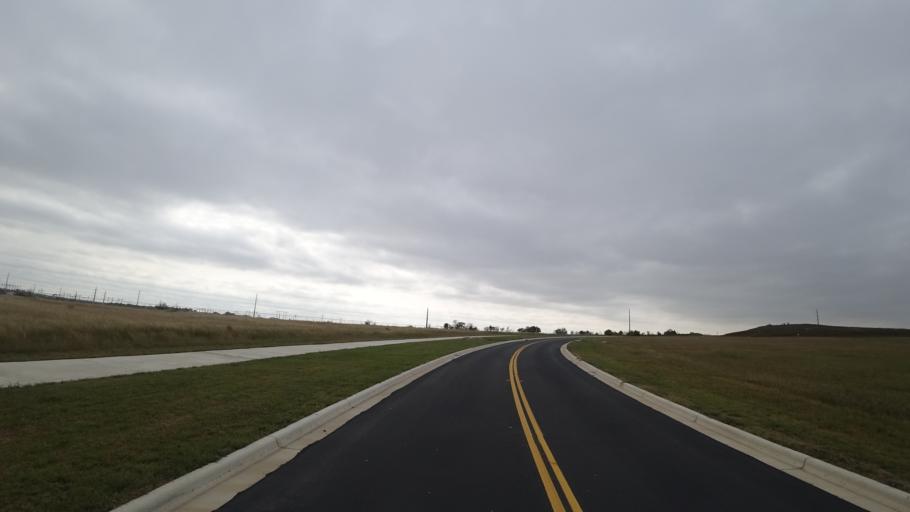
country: US
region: Texas
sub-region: Travis County
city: Pflugerville
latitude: 30.4129
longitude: -97.5905
